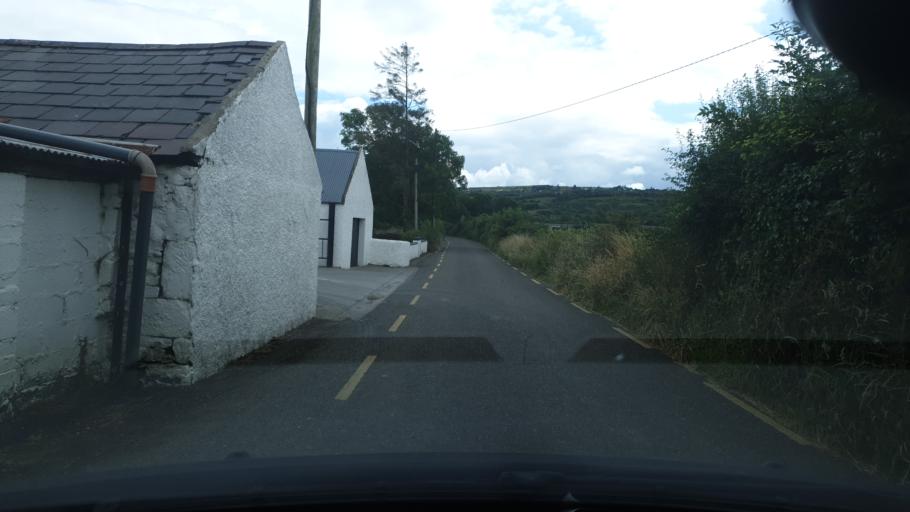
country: IE
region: Munster
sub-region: Ciarrai
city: Tralee
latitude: 52.2491
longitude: -9.6454
